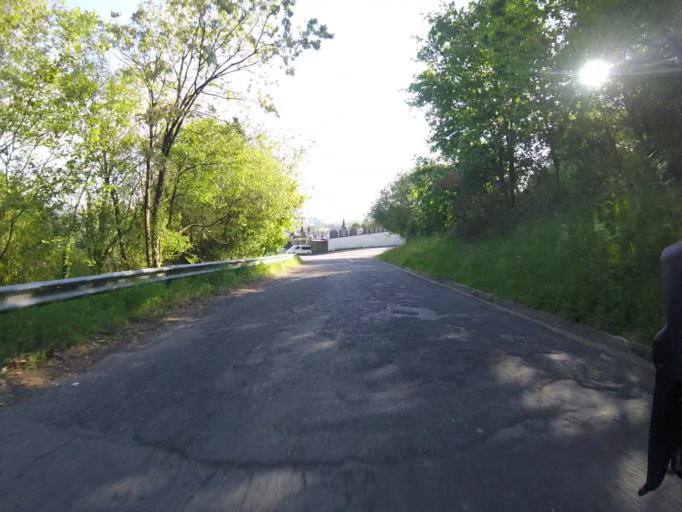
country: ES
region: Basque Country
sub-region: Provincia de Guipuzcoa
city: Pasaia
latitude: 43.3260
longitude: -1.9129
